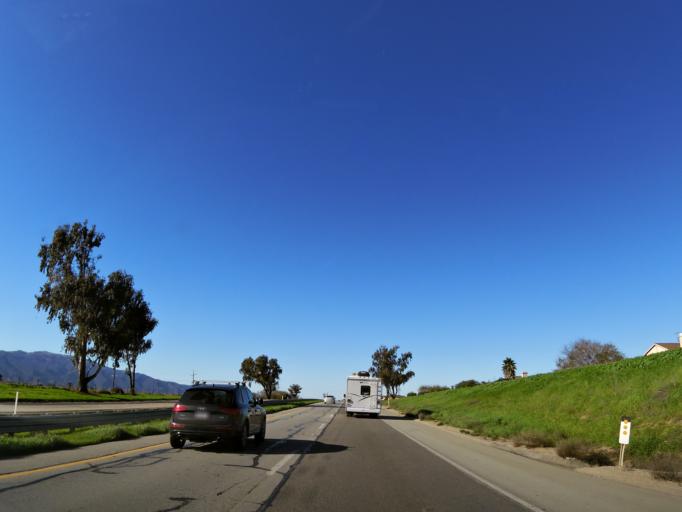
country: US
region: California
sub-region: Monterey County
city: Gonzales
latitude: 36.5188
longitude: -121.4422
